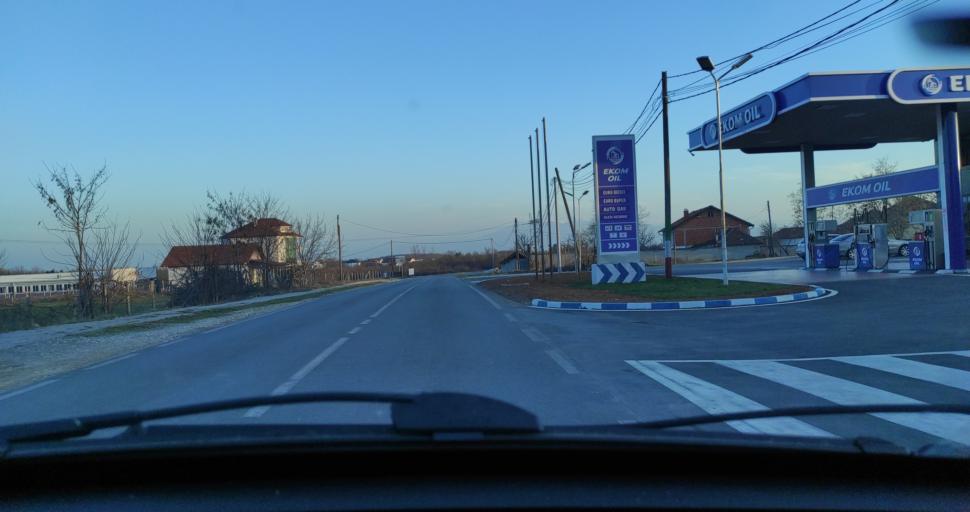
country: XK
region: Gjakova
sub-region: Komuna e Decanit
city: Gllogjan
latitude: 42.4690
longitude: 20.3447
